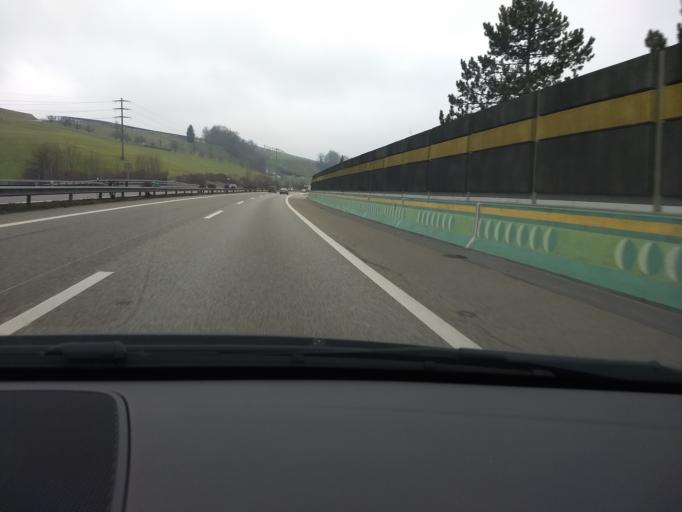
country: CH
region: Basel-Landschaft
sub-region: Bezirk Waldenburg
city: Diegten
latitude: 47.4039
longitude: 7.8072
